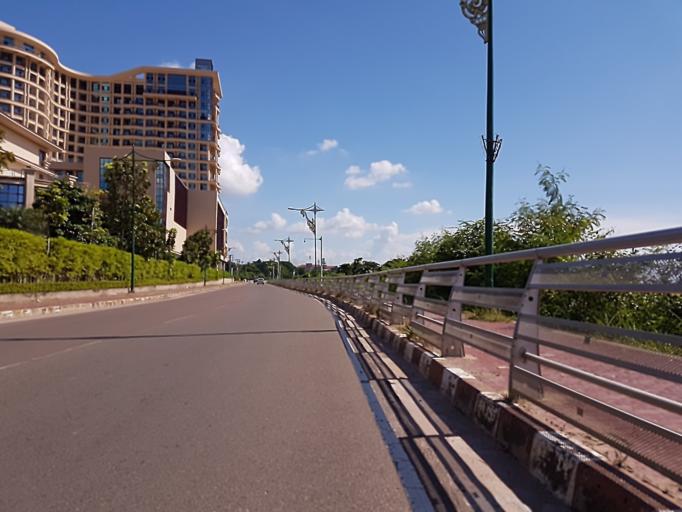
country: LA
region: Vientiane
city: Vientiane
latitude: 17.9438
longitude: 102.6162
